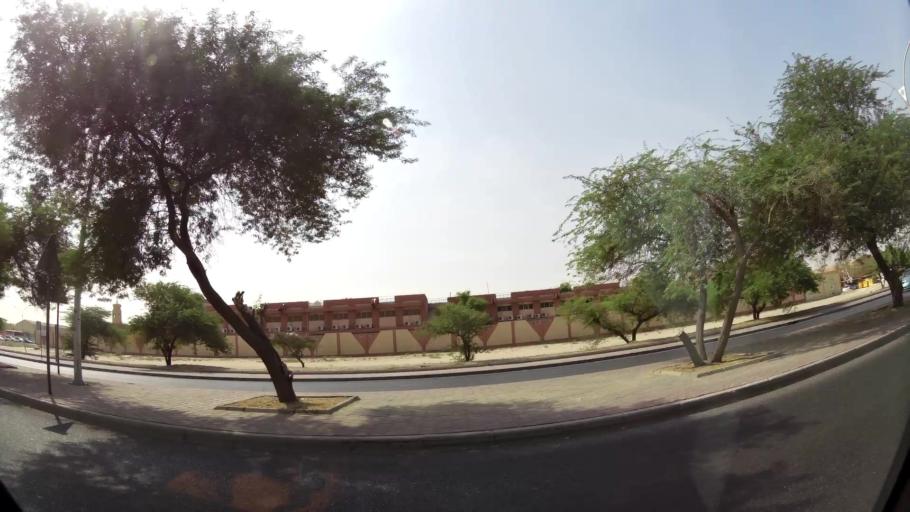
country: KW
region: Al Farwaniyah
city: Al Farwaniyah
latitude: 29.2492
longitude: 47.9311
